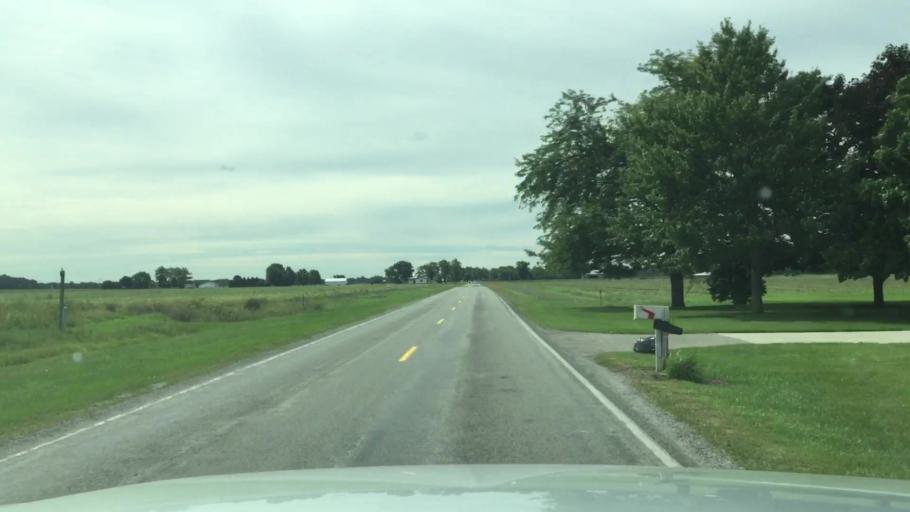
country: US
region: Michigan
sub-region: Genesee County
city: Montrose
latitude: 43.1389
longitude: -83.9882
